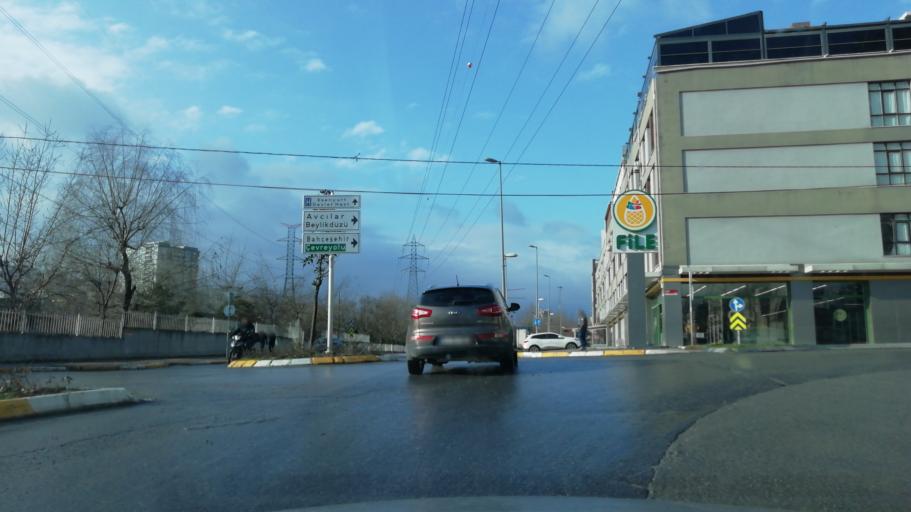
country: TR
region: Istanbul
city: Esenyurt
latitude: 41.0182
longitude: 28.6755
